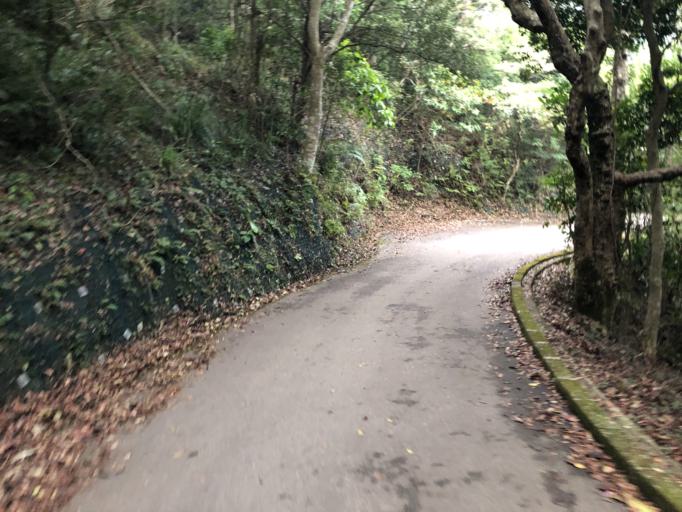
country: HK
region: Wanchai
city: Wan Chai
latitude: 22.2661
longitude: 114.2130
